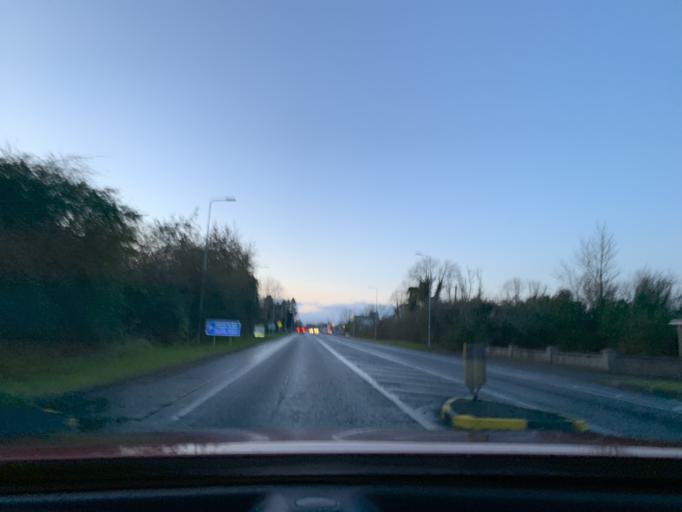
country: IE
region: Connaught
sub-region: County Leitrim
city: Carrick-on-Shannon
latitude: 53.9422
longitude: -8.0679
